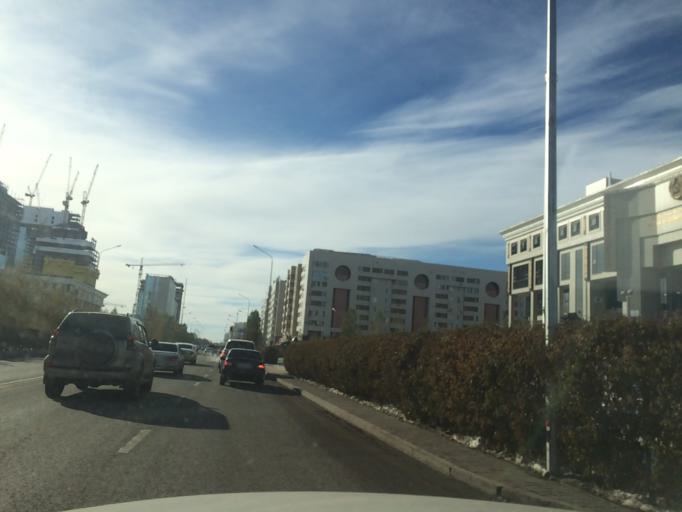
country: KZ
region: Astana Qalasy
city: Astana
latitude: 51.1275
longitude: 71.4281
